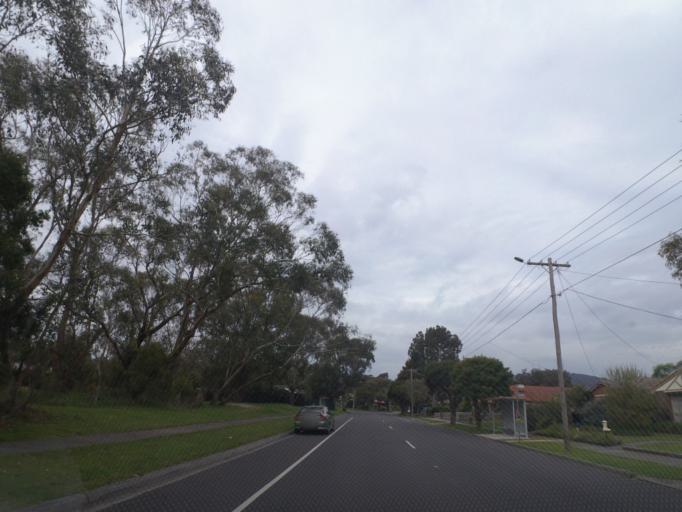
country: AU
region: Victoria
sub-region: Maroondah
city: Bayswater North
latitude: -37.8313
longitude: 145.2954
